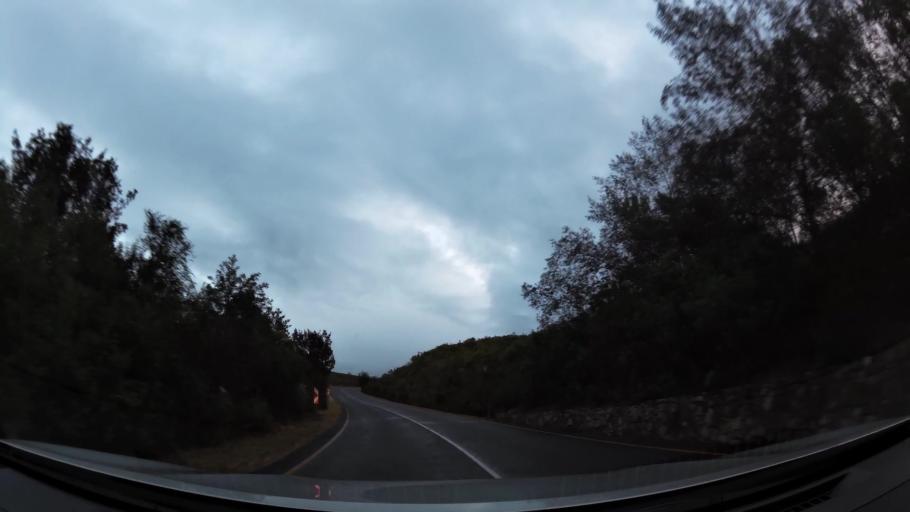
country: ZA
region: Western Cape
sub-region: Overberg District Municipality
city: Swellendam
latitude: -33.9855
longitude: 20.7183
